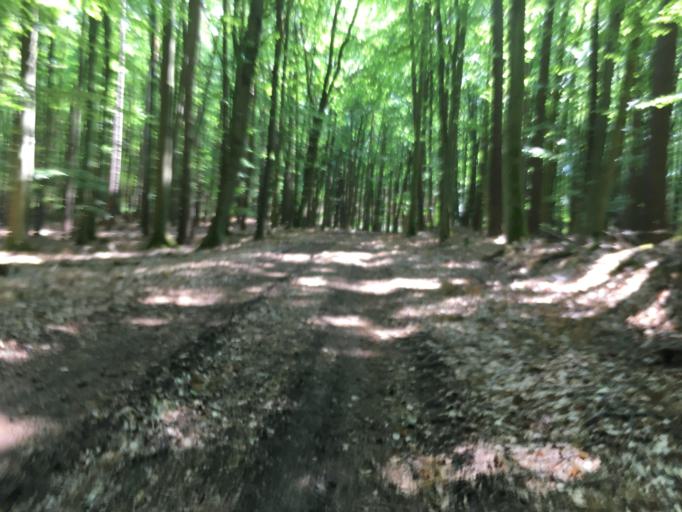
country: DE
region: Brandenburg
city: Joachimsthal
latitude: 53.0052
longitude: 13.7629
